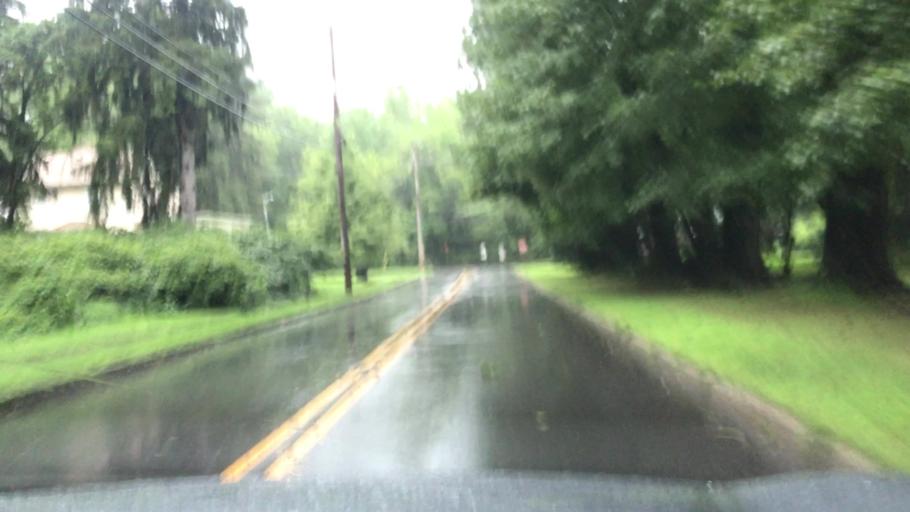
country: US
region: New Jersey
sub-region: Bergen County
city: Closter
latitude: 40.9815
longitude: -73.9613
